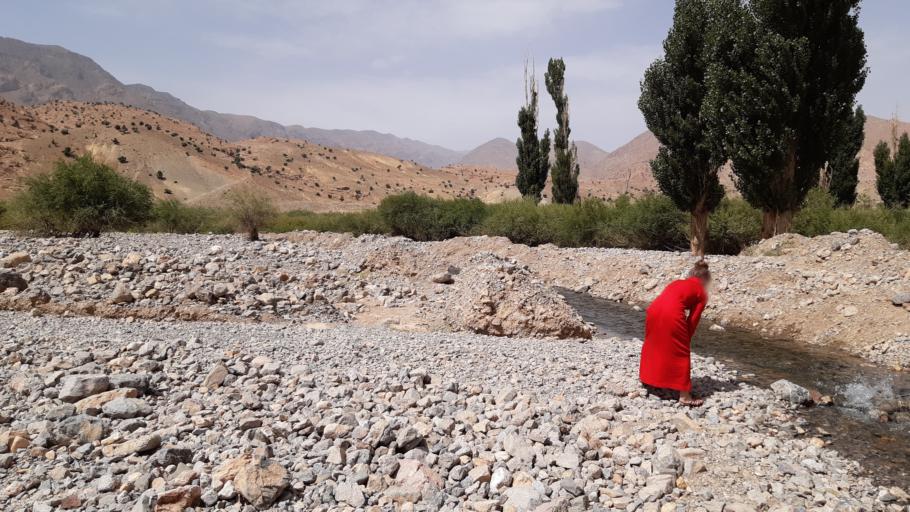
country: MA
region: Meknes-Tafilalet
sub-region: Khenifra
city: Midelt
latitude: 32.5841
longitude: -4.7680
